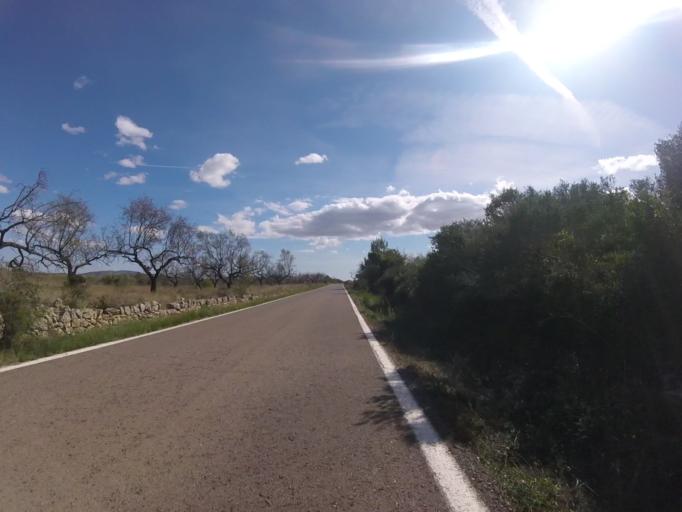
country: ES
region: Valencia
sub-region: Provincia de Castello
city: Albocasser
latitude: 40.4016
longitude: 0.0846
